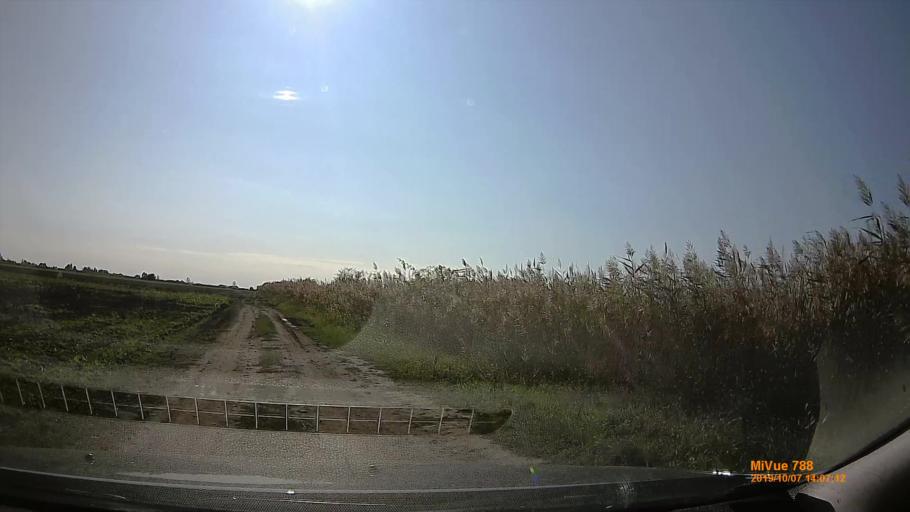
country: HU
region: Jasz-Nagykun-Szolnok
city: Cserkeszolo
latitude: 46.8732
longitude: 20.2266
